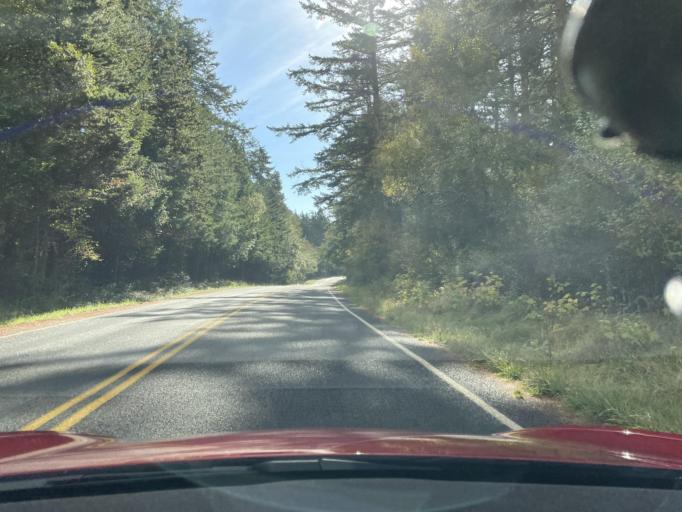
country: US
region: Washington
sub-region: San Juan County
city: Friday Harbor
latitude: 48.4699
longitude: -123.0323
